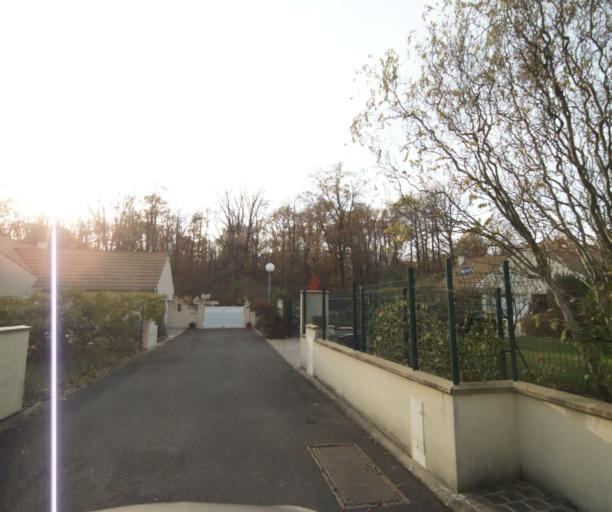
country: FR
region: Ile-de-France
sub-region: Departement des Yvelines
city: Chanteloup-les-Vignes
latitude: 48.9923
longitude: 2.0215
